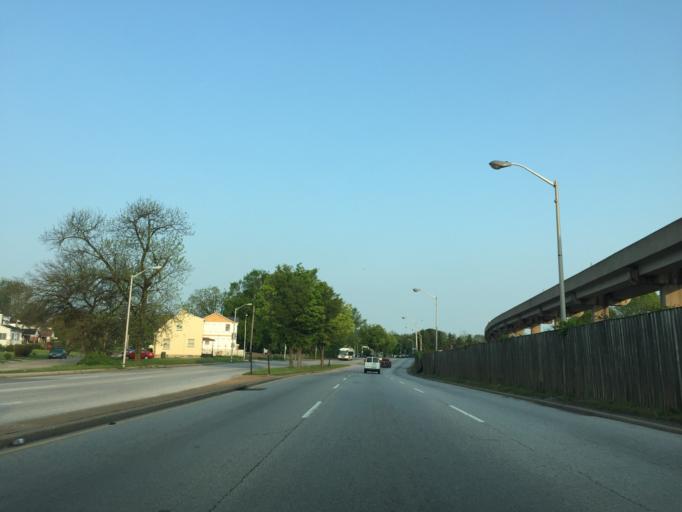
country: US
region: Maryland
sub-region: Baltimore County
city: Lochearn
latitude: 39.3419
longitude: -76.6855
